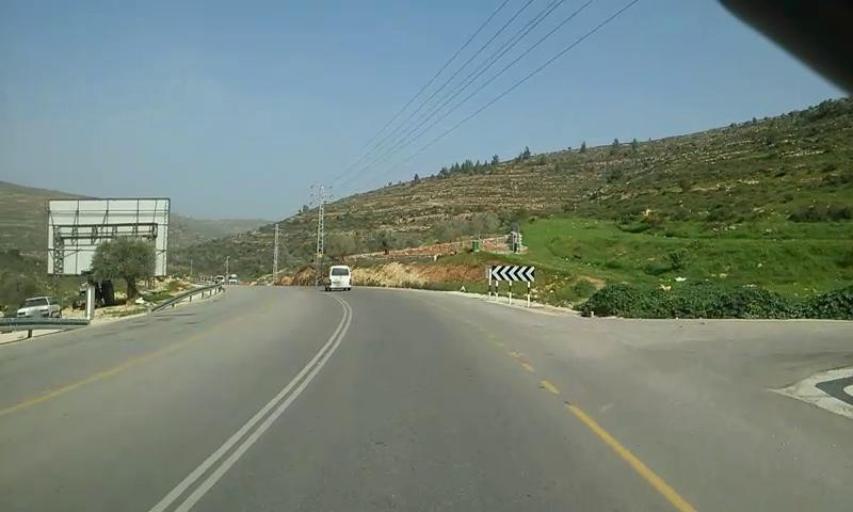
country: PS
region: West Bank
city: Dura al Qar`
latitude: 31.9821
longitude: 35.2347
